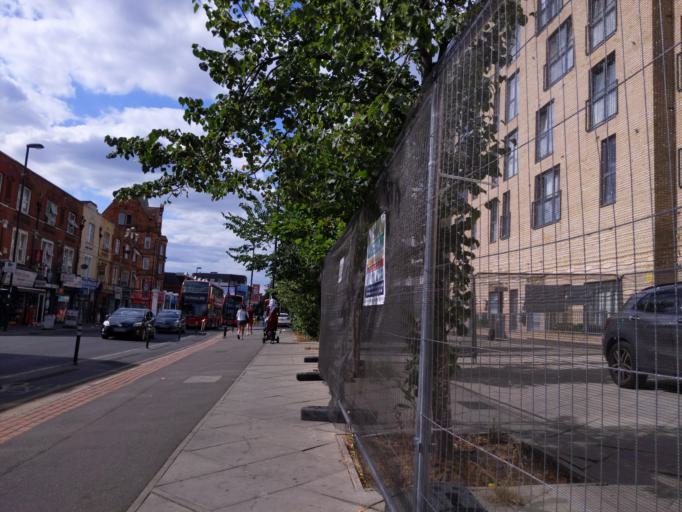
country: GB
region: England
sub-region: Greater London
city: Croydon
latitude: 51.3848
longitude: -0.1091
